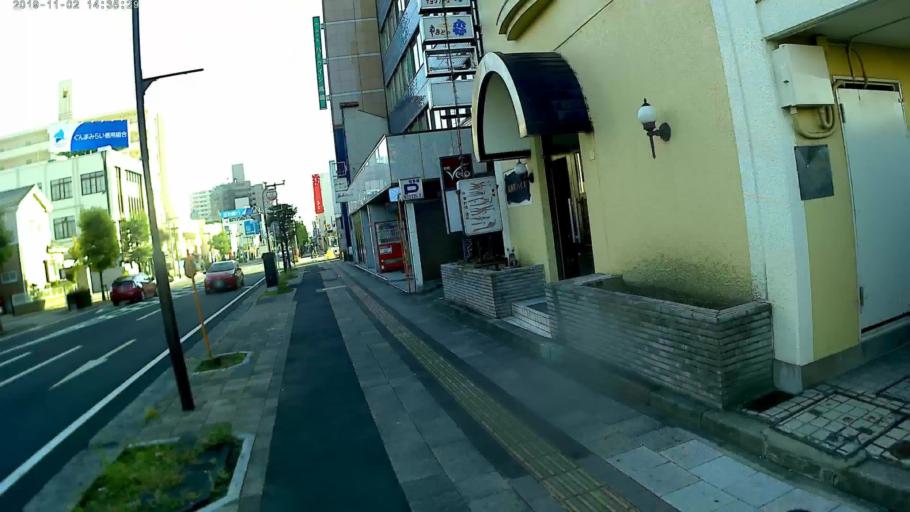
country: JP
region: Gunma
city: Takasaki
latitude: 36.3294
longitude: 139.0063
